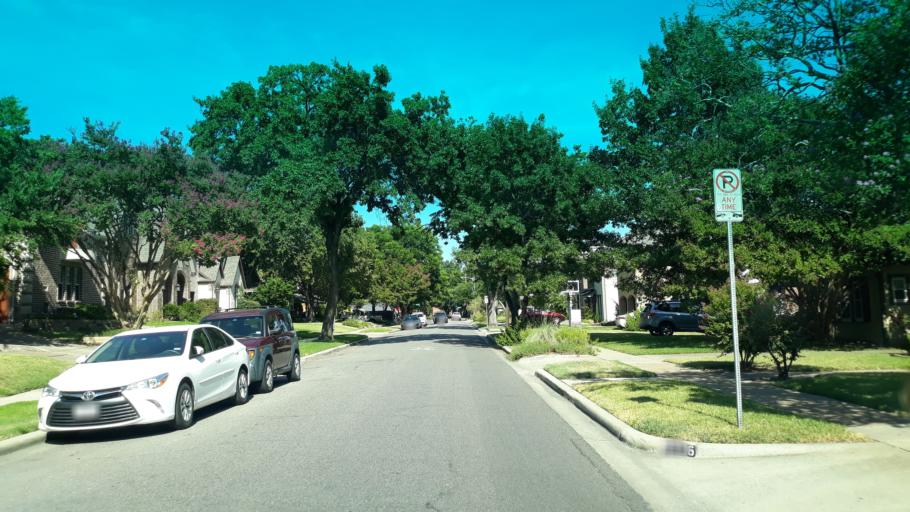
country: US
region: Texas
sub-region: Dallas County
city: Highland Park
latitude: 32.8172
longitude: -96.7549
